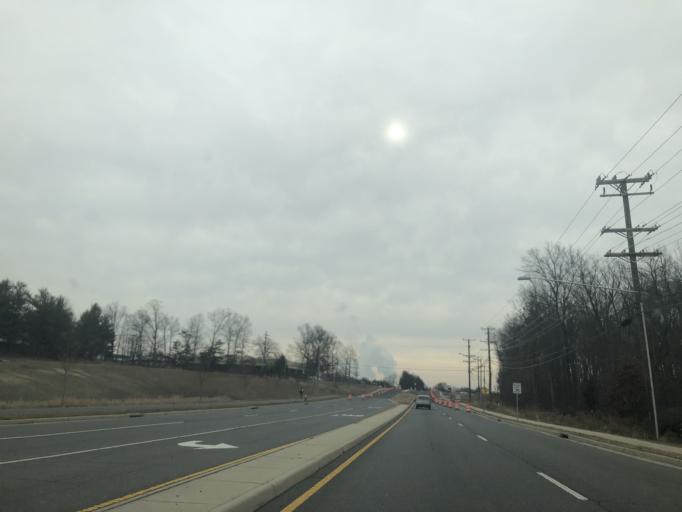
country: US
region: Virginia
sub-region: Loudoun County
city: Leesburg
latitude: 39.0868
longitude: -77.5532
